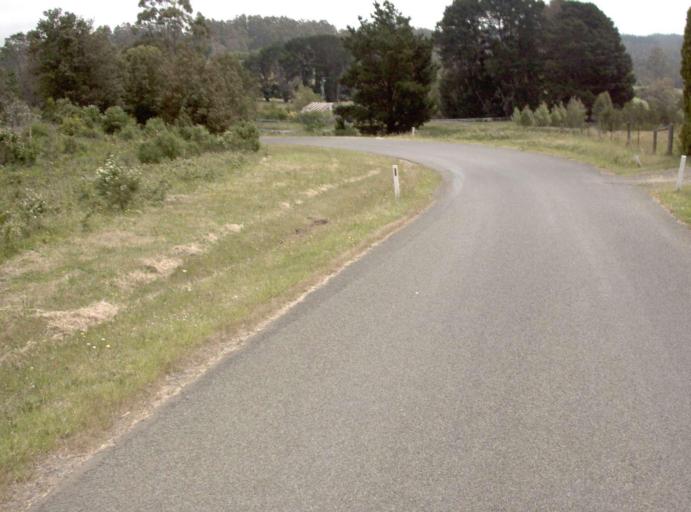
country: AU
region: Victoria
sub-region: Latrobe
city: Traralgon
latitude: -38.4200
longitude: 146.6095
